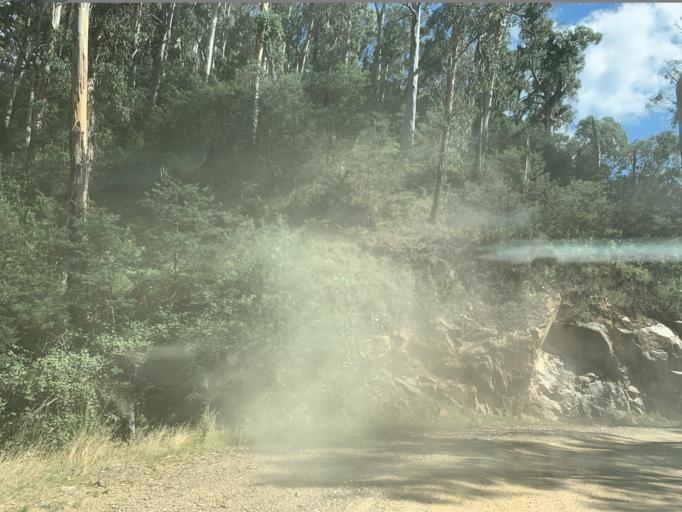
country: AU
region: Victoria
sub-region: Mansfield
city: Mansfield
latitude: -37.0942
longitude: 146.5281
